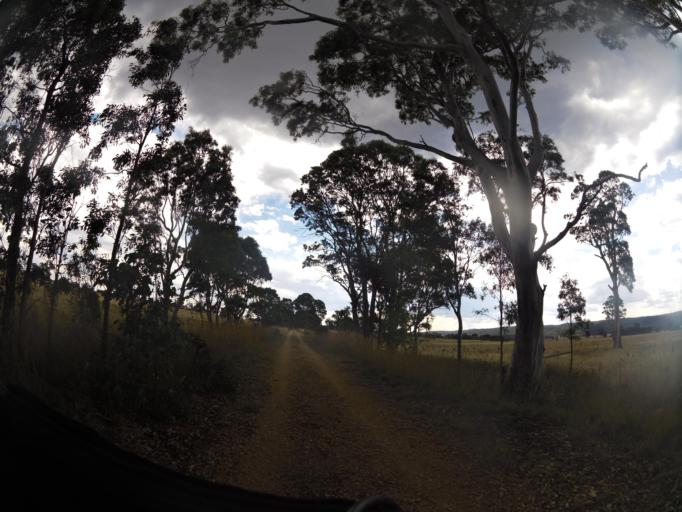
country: AU
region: Victoria
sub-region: Wellington
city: Heyfield
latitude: -38.0224
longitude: 146.6765
